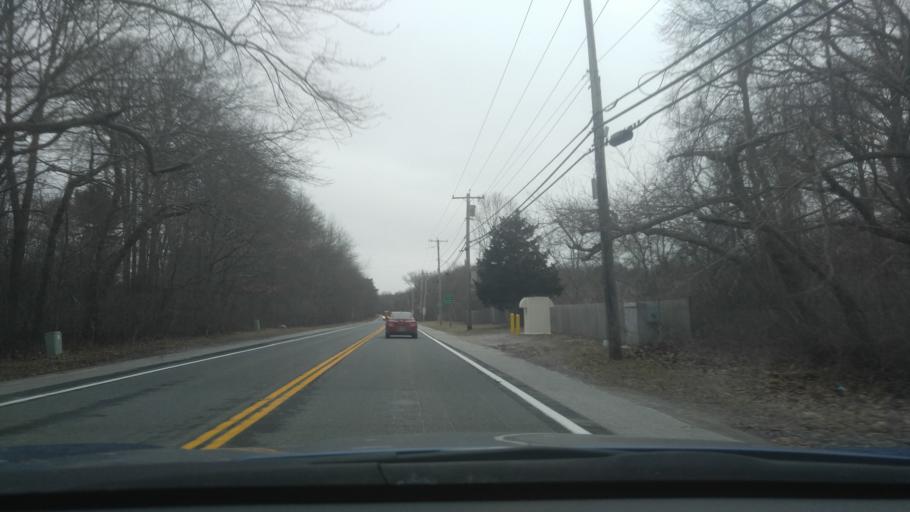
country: US
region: Rhode Island
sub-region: Washington County
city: North Kingstown
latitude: 41.5033
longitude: -71.4306
